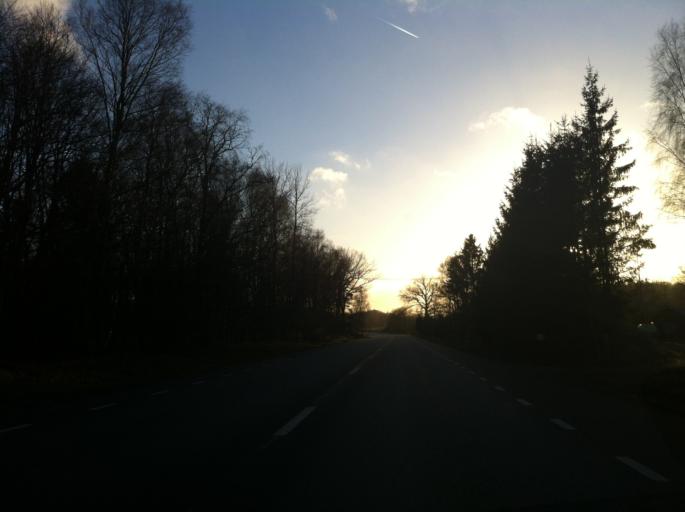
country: SE
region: Skane
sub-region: Hassleholms Kommun
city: Hassleholm
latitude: 56.1324
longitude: 13.7993
